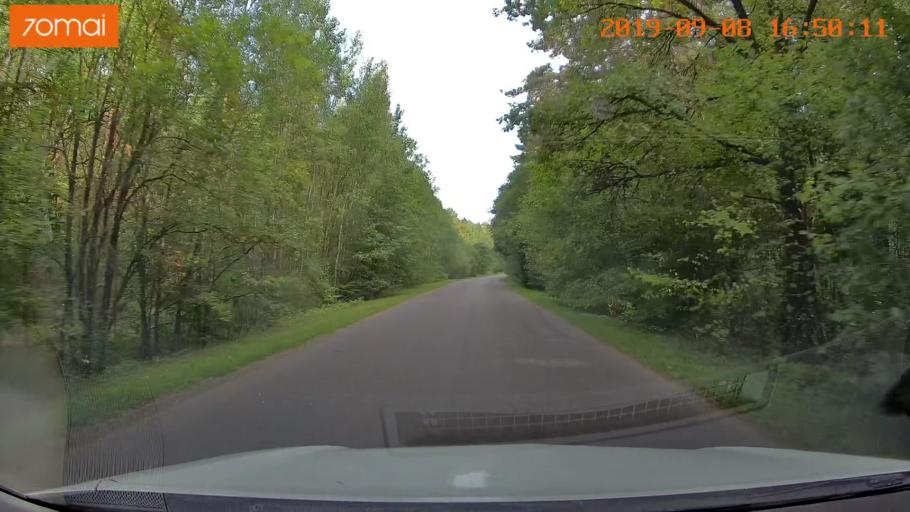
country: BY
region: Grodnenskaya
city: Hrodna
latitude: 53.8026
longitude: 23.8853
